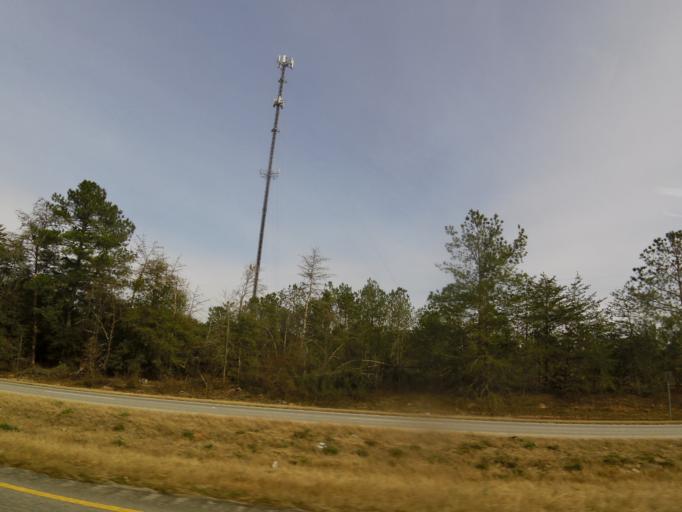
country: US
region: Alabama
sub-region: Dale County
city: Newton
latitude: 31.3459
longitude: -85.5524
